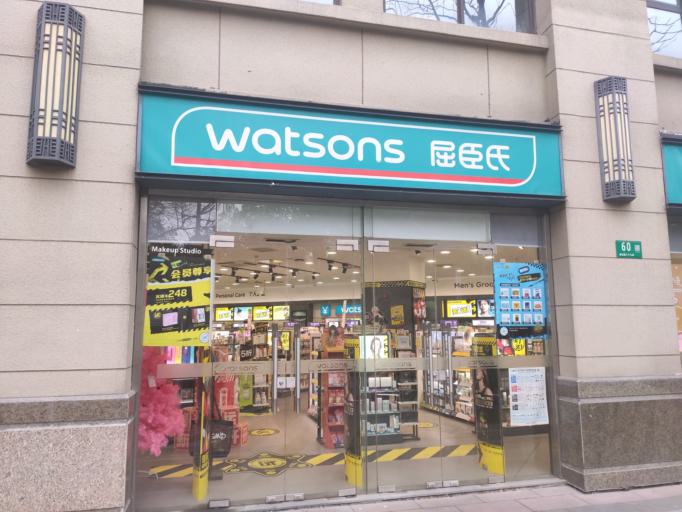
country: CN
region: Shanghai Shi
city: Huacao
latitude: 31.2097
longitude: 121.2868
